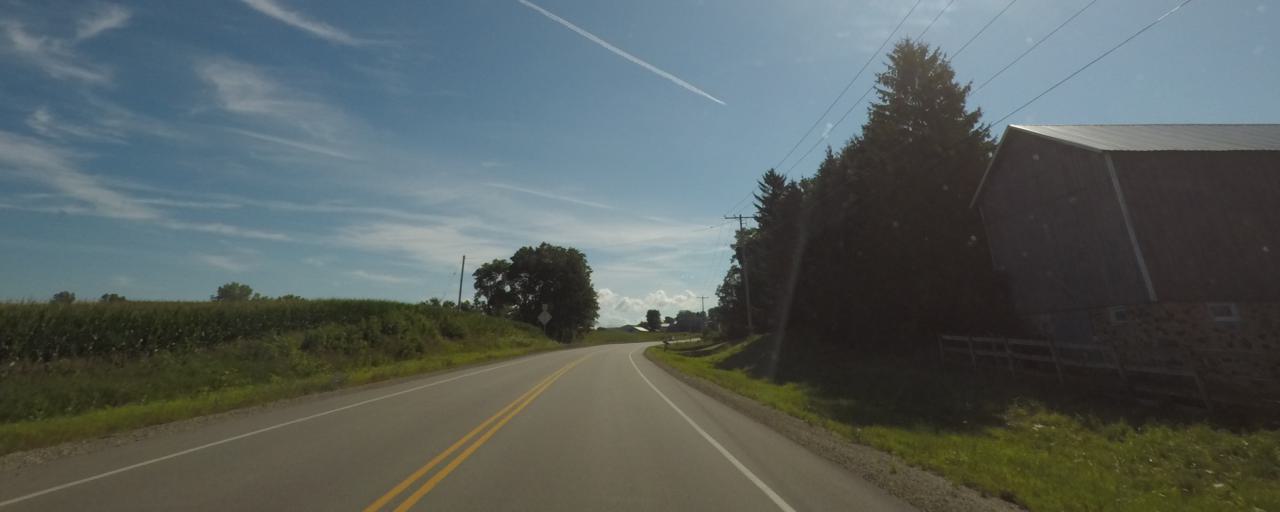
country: US
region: Wisconsin
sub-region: Jefferson County
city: Johnson Creek
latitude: 43.0750
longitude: -88.6788
